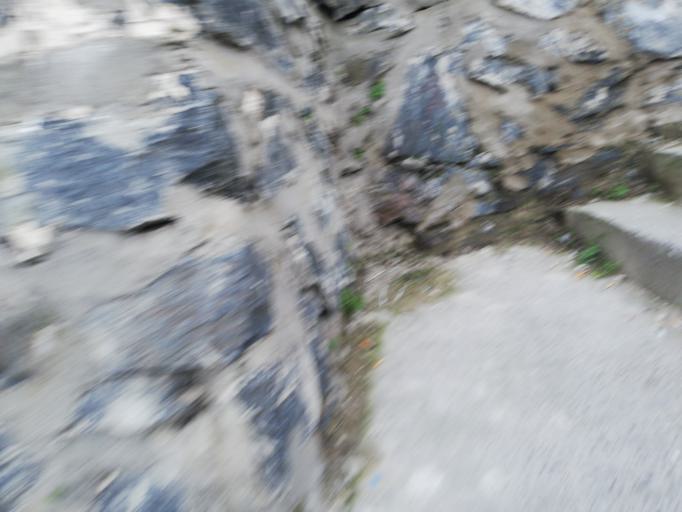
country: TR
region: Istanbul
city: Sisli
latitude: 41.0856
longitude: 28.9719
